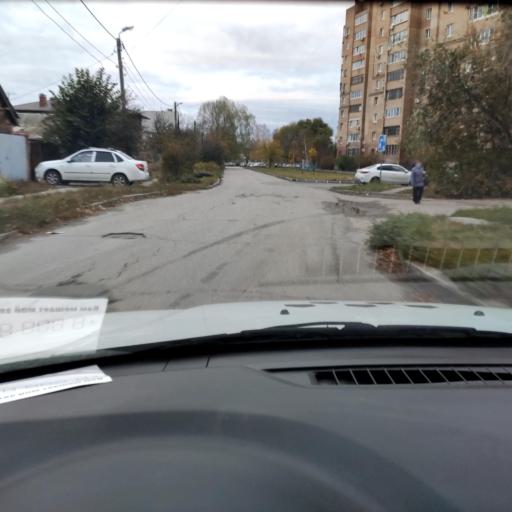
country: RU
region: Samara
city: Tol'yatti
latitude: 53.5230
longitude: 49.4179
